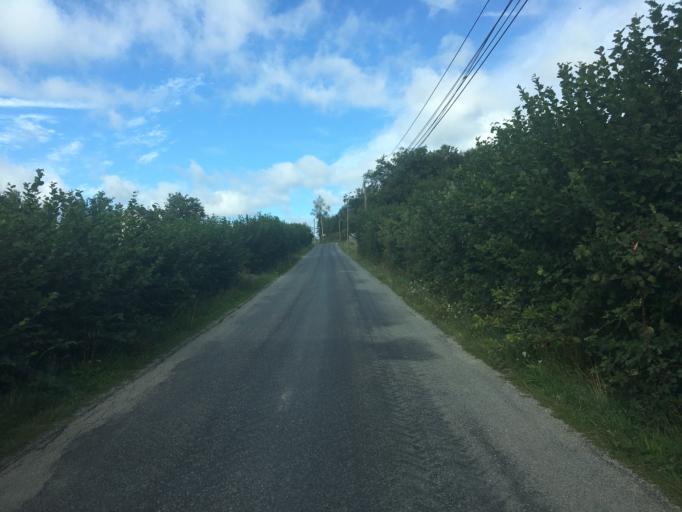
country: FR
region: Auvergne
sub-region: Departement du Cantal
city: Champagnac
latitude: 45.4147
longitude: 2.4262
